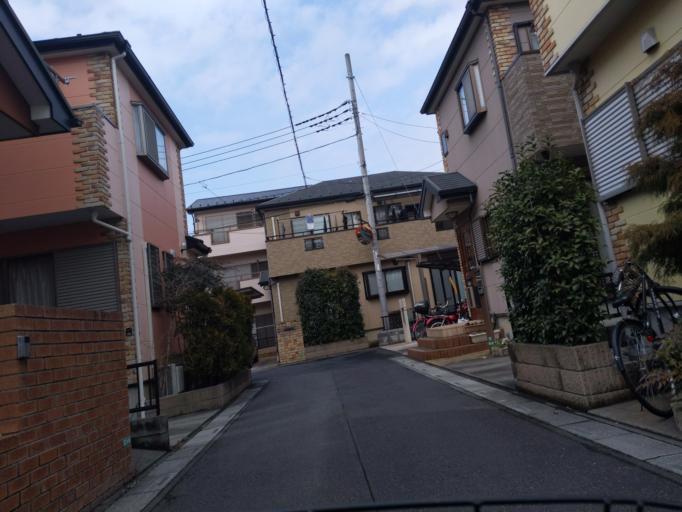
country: JP
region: Saitama
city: Soka
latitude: 35.8472
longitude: 139.7947
